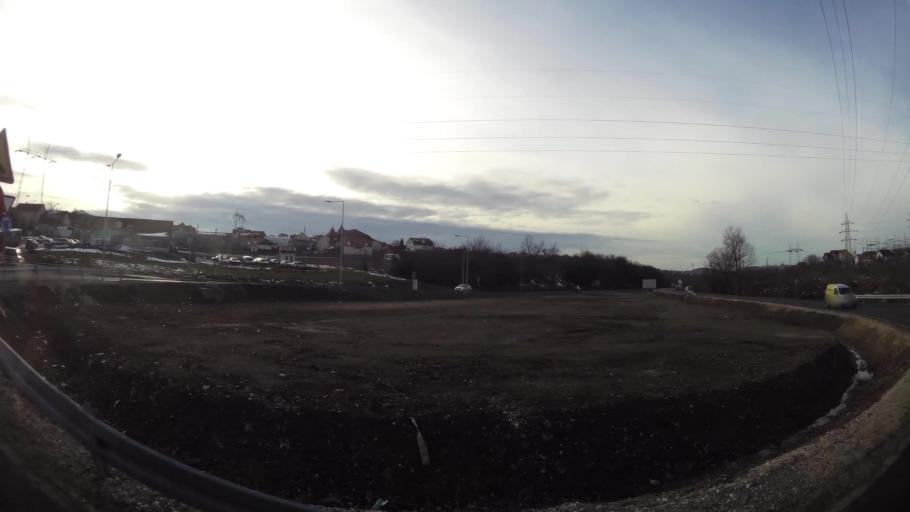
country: RS
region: Central Serbia
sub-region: Belgrade
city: Rakovica
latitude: 44.7174
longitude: 20.4664
